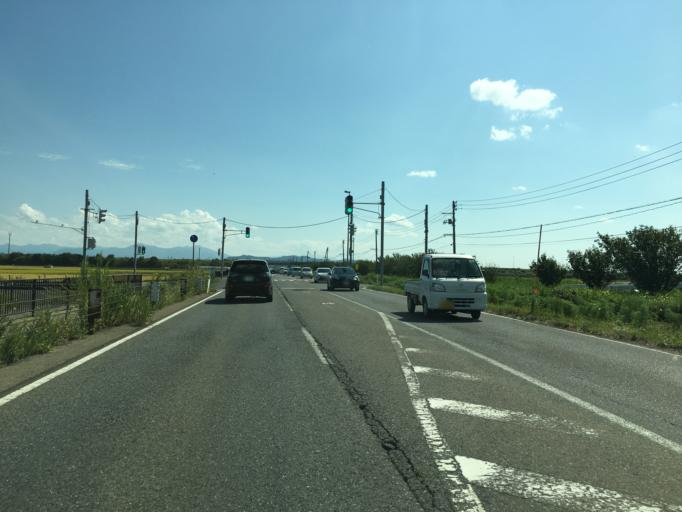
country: JP
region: Niigata
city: Niitsu-honcho
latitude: 37.8257
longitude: 139.0981
